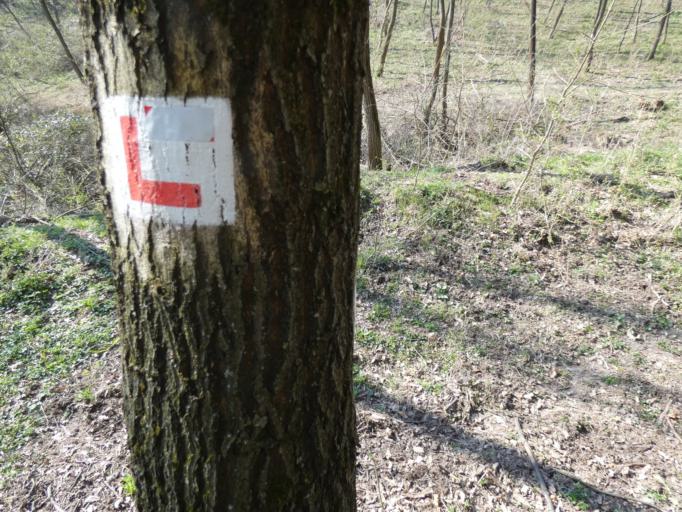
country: HU
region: Pest
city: Szob
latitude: 47.8626
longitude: 18.8567
